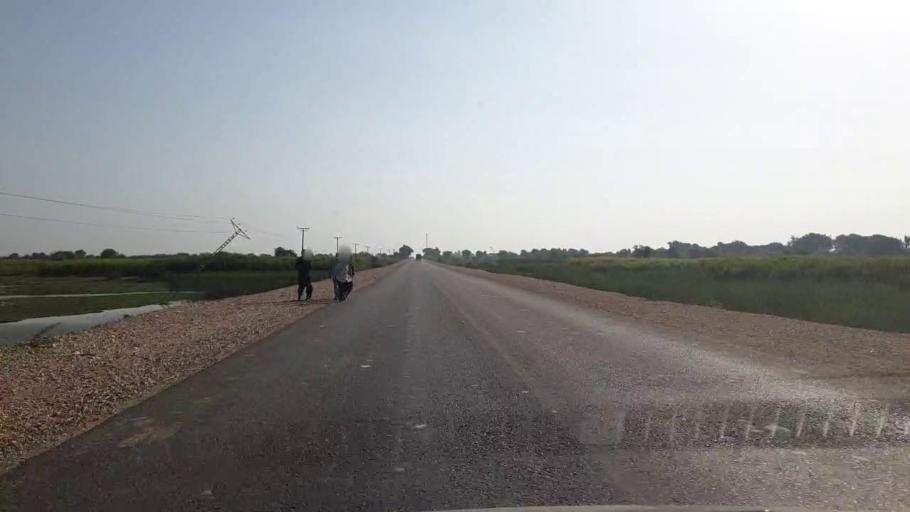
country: PK
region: Sindh
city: Badin
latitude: 24.6588
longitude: 68.9381
